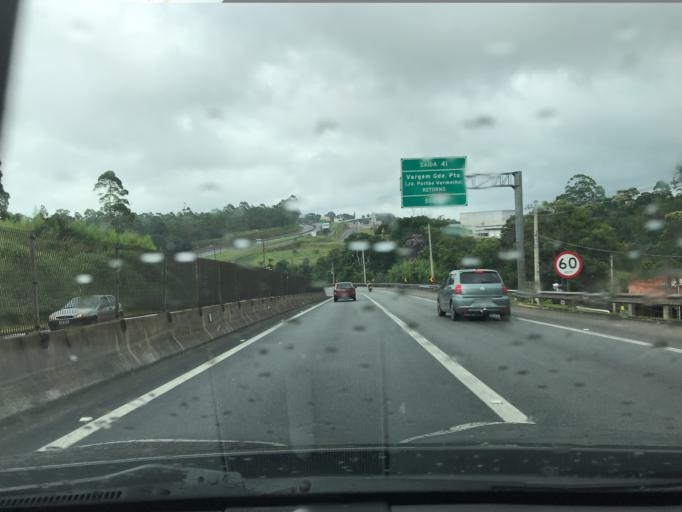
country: BR
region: Sao Paulo
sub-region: Vargem Grande Paulista
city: Vargem Grande Paulista
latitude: -23.6122
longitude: -46.9855
